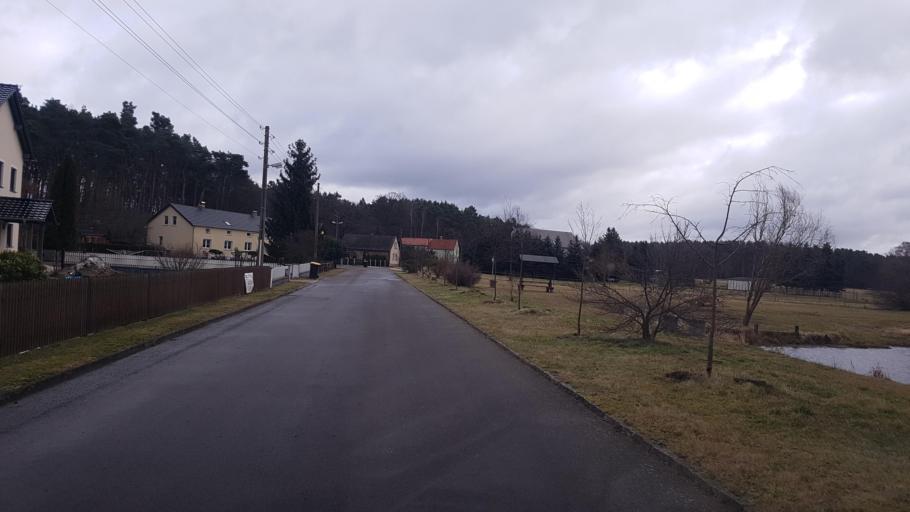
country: DE
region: Brandenburg
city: Kroppen
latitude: 51.3783
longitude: 13.8009
